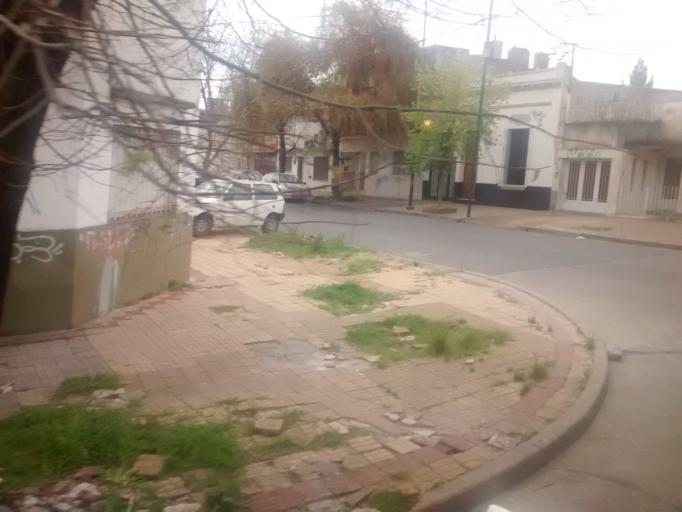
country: AR
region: Buenos Aires
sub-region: Partido de La Plata
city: La Plata
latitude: -34.9314
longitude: -57.9345
